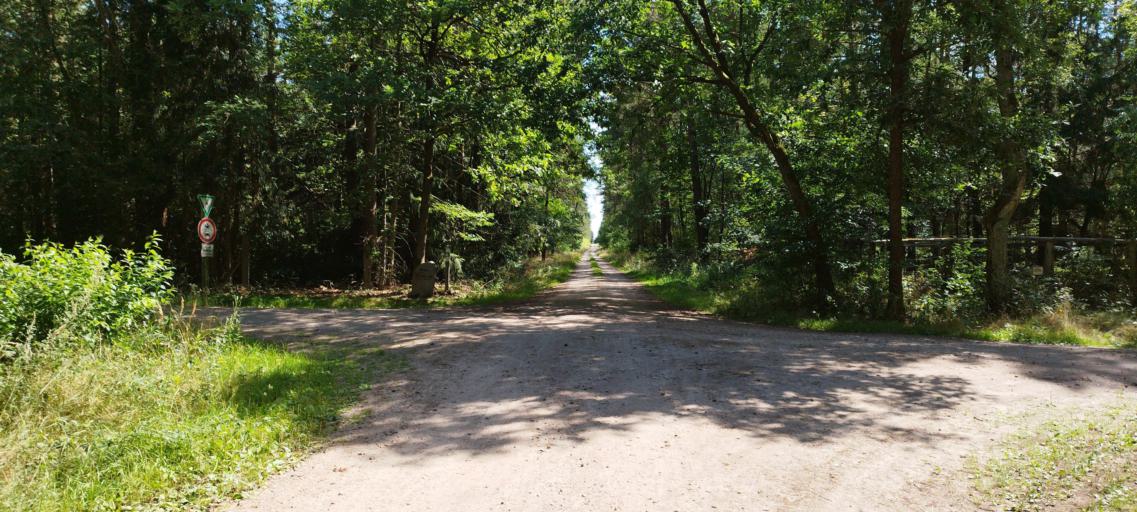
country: DE
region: Lower Saxony
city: Fassberg
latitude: 52.8442
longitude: 10.1935
